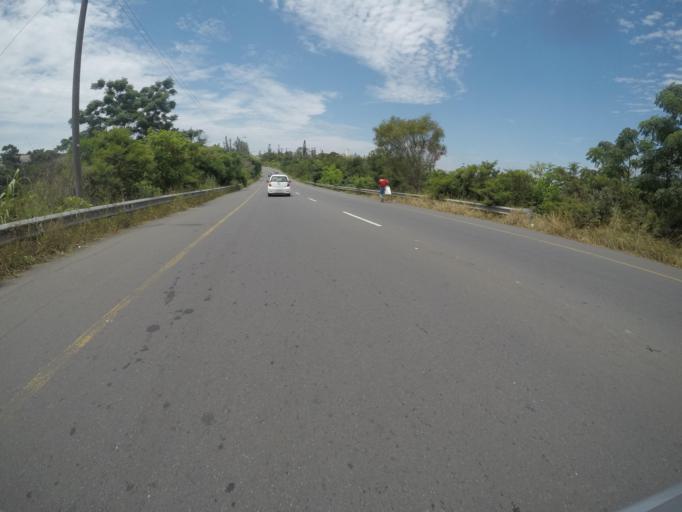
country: ZA
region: Eastern Cape
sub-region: Buffalo City Metropolitan Municipality
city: East London
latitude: -32.9826
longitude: 27.8707
